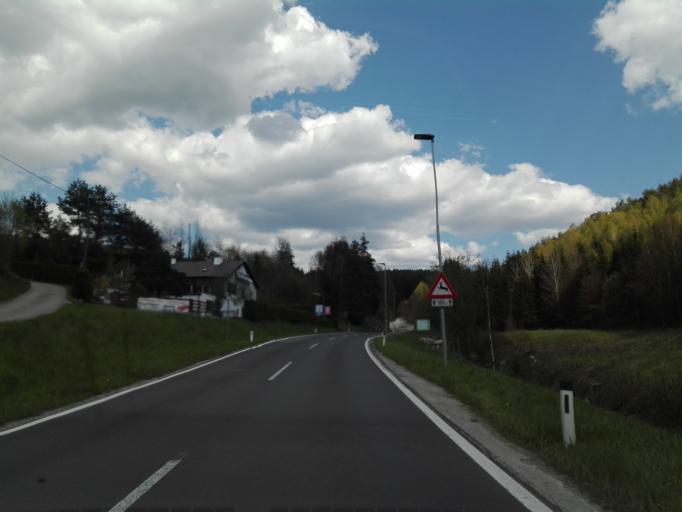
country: AT
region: Upper Austria
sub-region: Politischer Bezirk Freistadt
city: Freistadt
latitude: 48.5199
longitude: 14.5179
